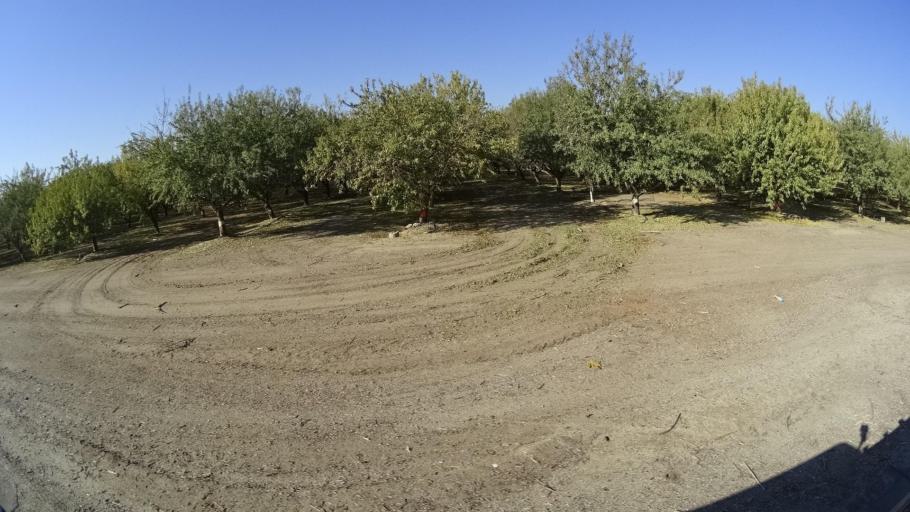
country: US
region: California
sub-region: Kern County
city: Delano
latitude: 35.7575
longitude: -119.2233
